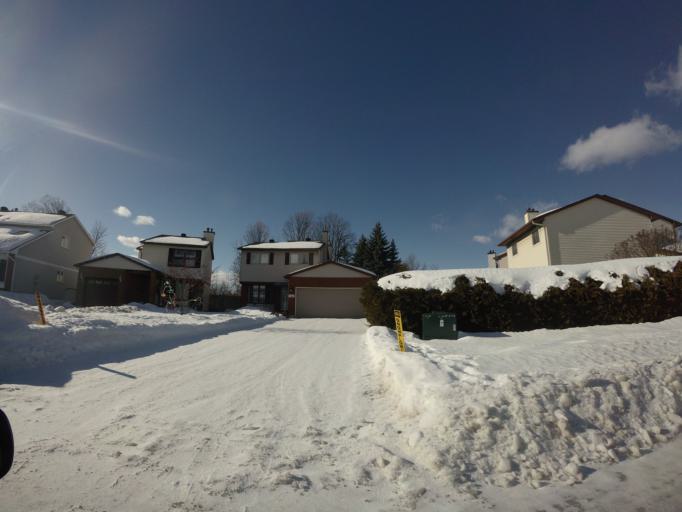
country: CA
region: Ontario
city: Ottawa
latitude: 45.4233
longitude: -75.6137
